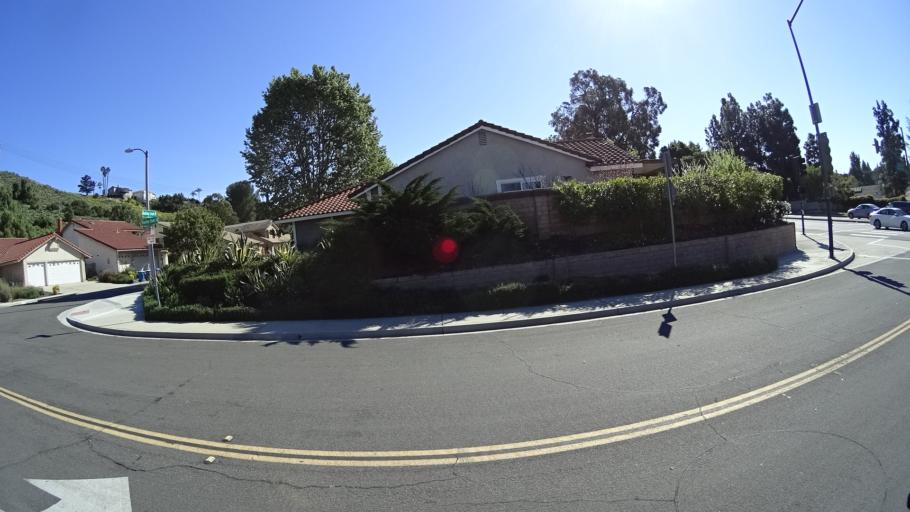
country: US
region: California
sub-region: Ventura County
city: Moorpark
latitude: 34.2301
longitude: -118.8667
